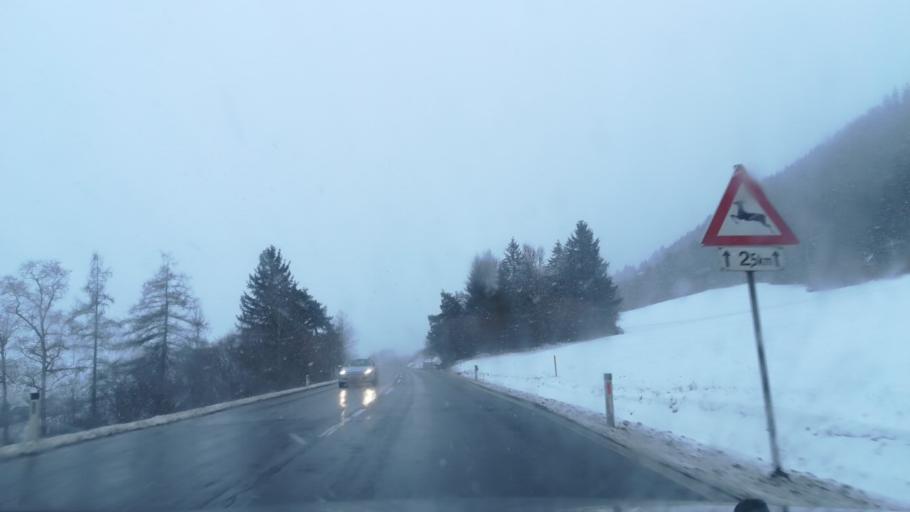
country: AT
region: Styria
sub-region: Politischer Bezirk Murtal
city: Sankt Peter ob Judenburg
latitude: 47.1970
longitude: 14.5948
